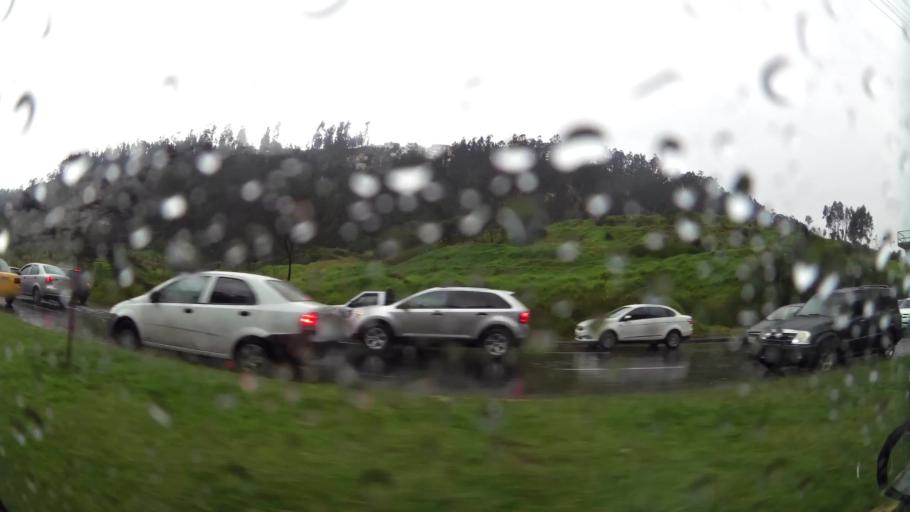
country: EC
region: Pichincha
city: Quito
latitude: -0.1502
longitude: -78.4539
